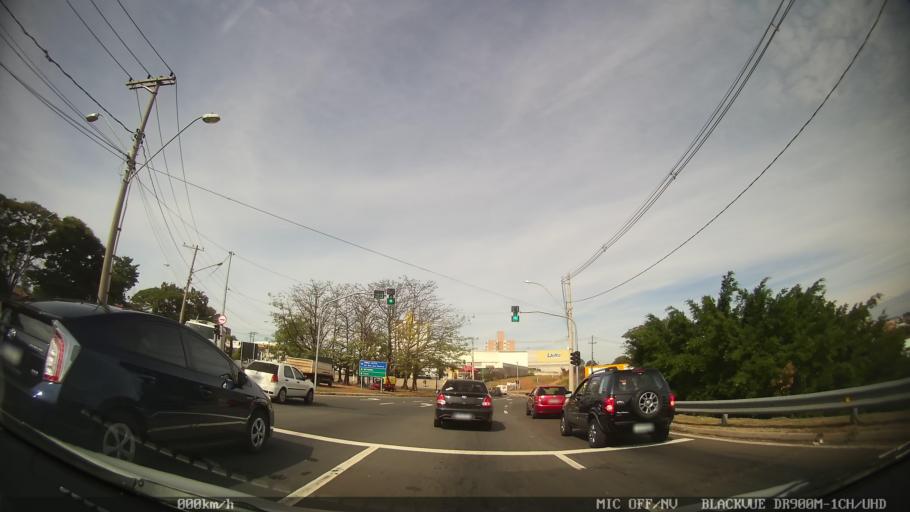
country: BR
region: Sao Paulo
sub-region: Piracicaba
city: Piracicaba
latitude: -22.7452
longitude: -47.6395
